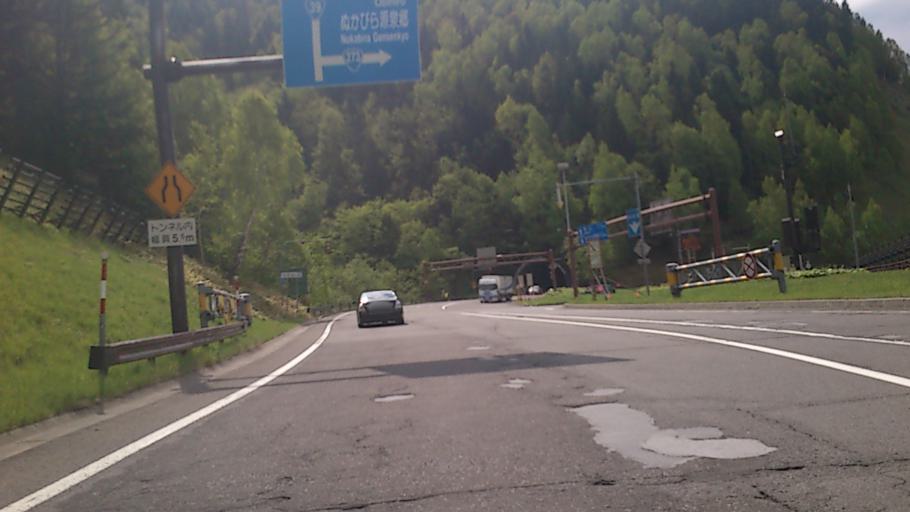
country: JP
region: Hokkaido
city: Kamikawa
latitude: 43.6813
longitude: 143.0361
